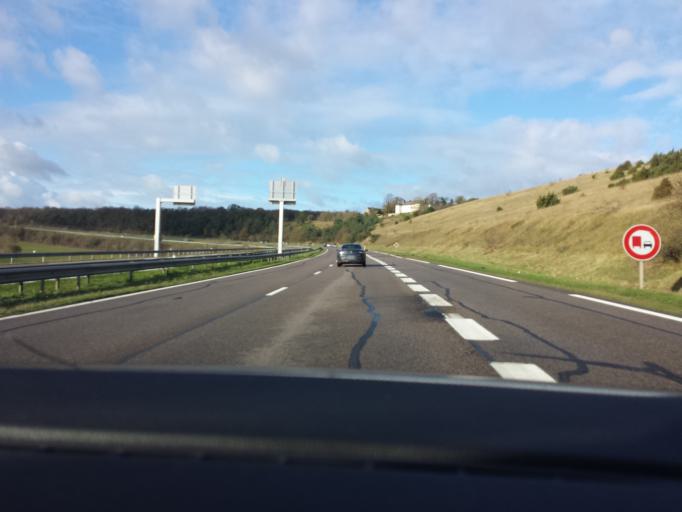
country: FR
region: Haute-Normandie
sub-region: Departement de l'Eure
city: Menilles
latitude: 49.0127
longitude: 1.3518
